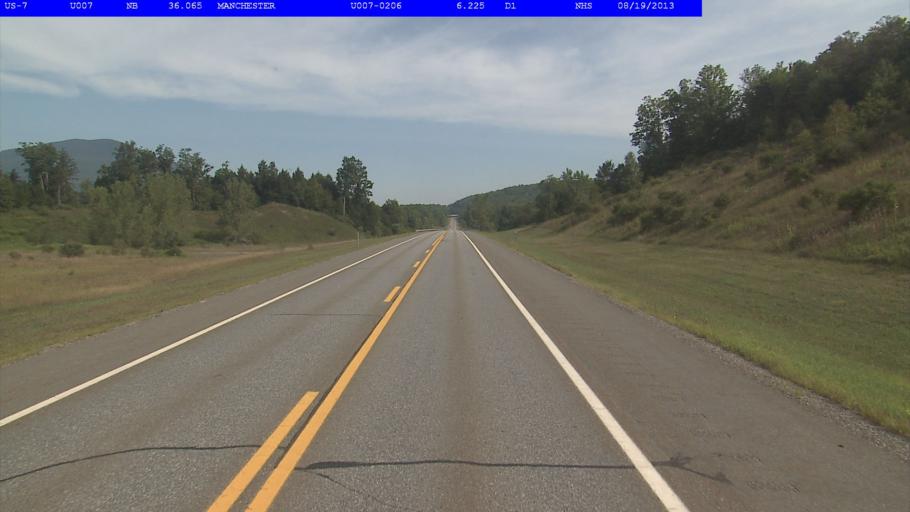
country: US
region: Vermont
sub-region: Bennington County
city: Manchester Center
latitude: 43.1922
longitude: -73.0139
